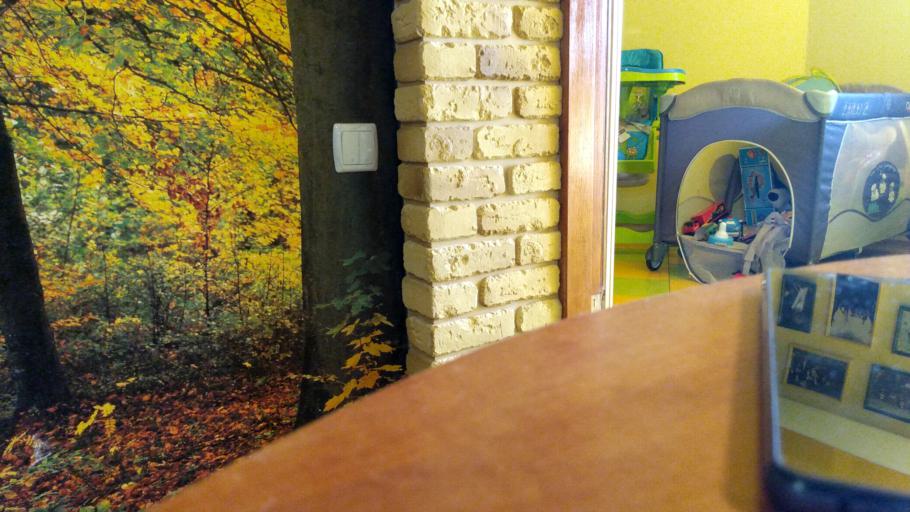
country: RU
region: Tverskaya
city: Kalashnikovo
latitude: 57.3722
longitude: 35.2079
